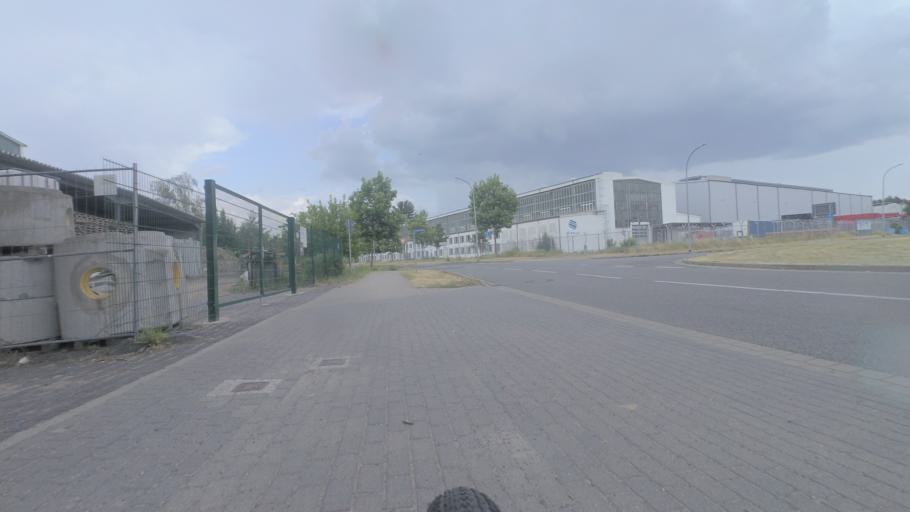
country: DE
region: Brandenburg
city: Ludwigsfelde
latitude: 52.3206
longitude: 13.2573
